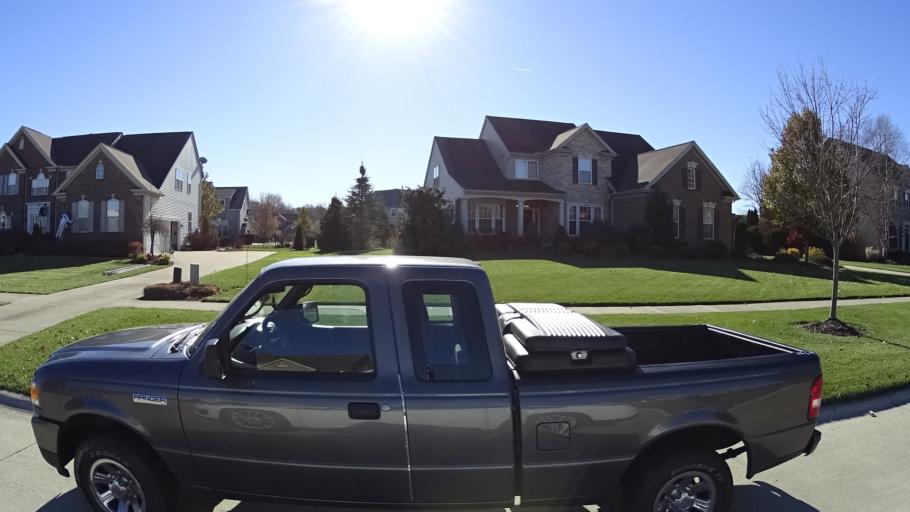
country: US
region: Ohio
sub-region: Lorain County
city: Avon
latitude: 41.4292
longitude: -82.0312
